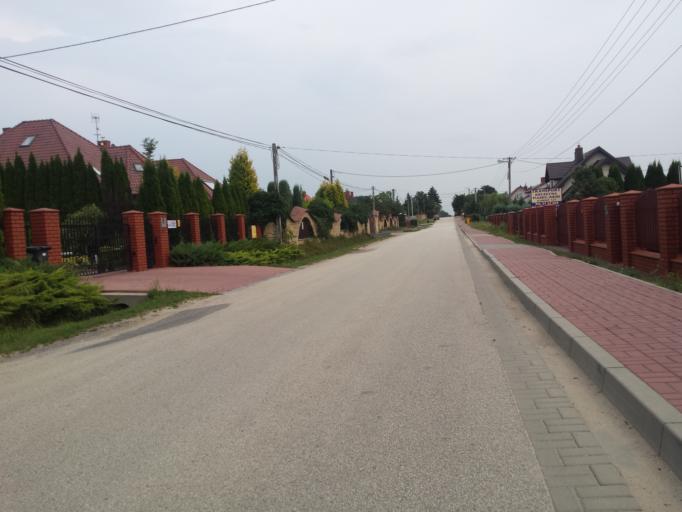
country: PL
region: Swietokrzyskie
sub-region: Powiat kielecki
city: Morawica
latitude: 50.7677
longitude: 20.6296
